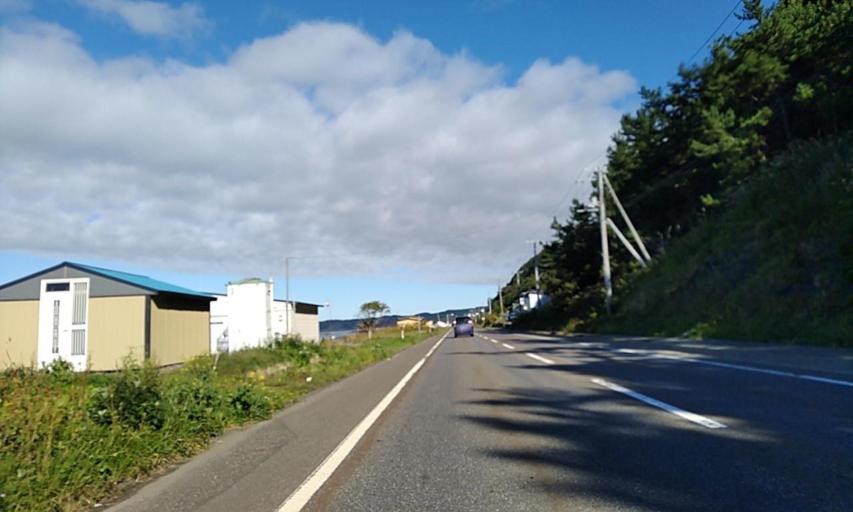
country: JP
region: Hokkaido
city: Shizunai-furukawacho
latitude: 42.2850
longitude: 142.4643
